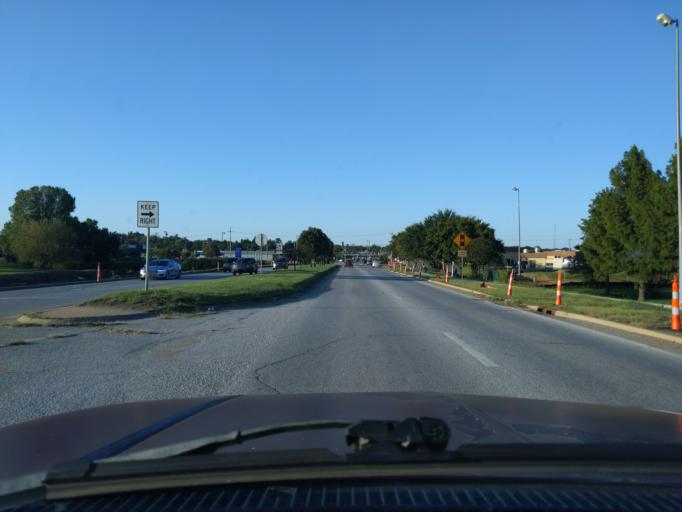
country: US
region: Oklahoma
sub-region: Tulsa County
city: Sand Springs
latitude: 36.1314
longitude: -96.1160
